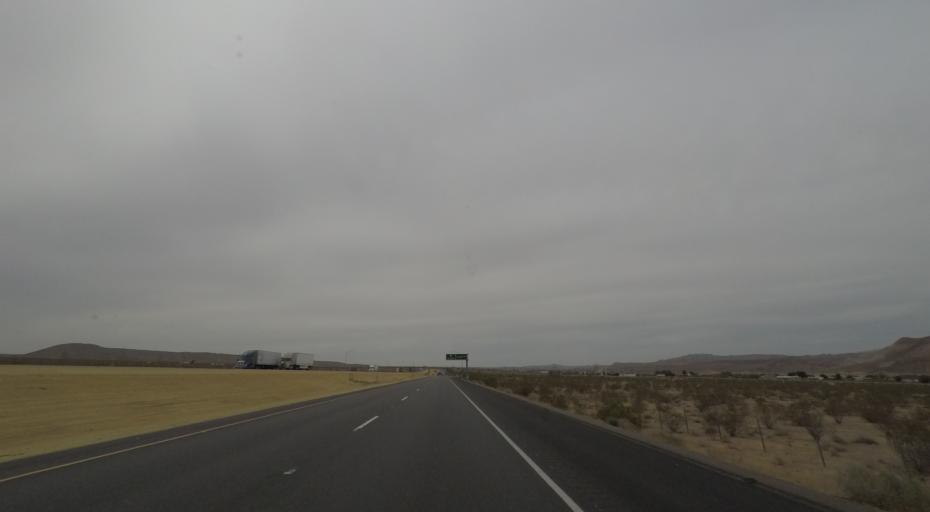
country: US
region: California
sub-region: San Bernardino County
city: Barstow
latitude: 34.8536
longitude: -116.8822
